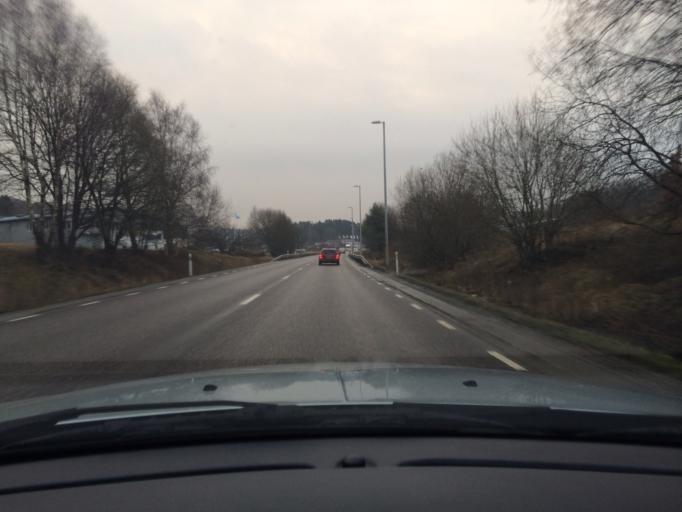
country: SE
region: Vaestra Goetaland
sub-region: Stenungsunds Kommun
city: Stenungsund
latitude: 58.0665
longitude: 11.8639
